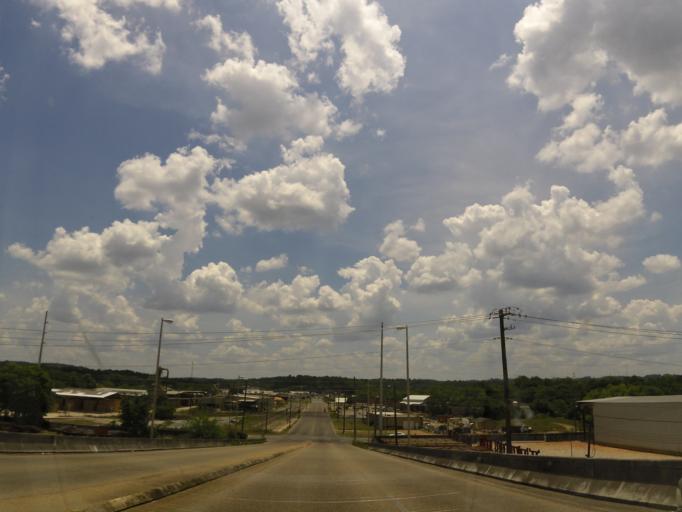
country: US
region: Mississippi
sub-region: Lauderdale County
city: Meridian
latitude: 32.3636
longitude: -88.6940
